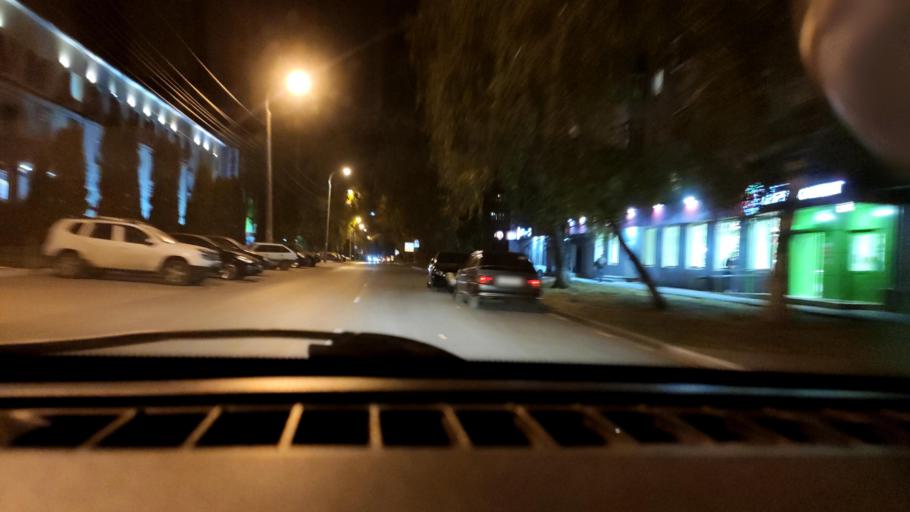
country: RU
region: Samara
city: Samara
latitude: 53.2015
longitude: 50.1743
